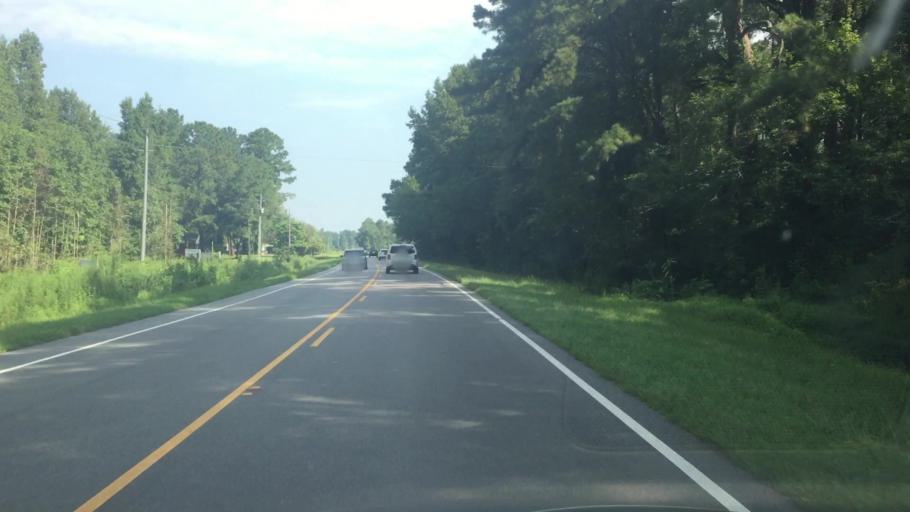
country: US
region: North Carolina
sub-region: Columbus County
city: Chadbourn
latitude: 34.3456
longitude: -78.8274
